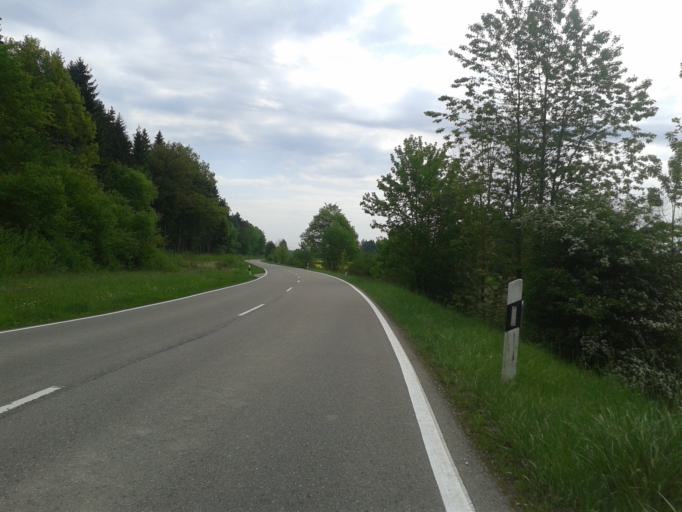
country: DE
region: Baden-Wuerttemberg
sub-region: Tuebingen Region
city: Erbach
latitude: 48.3542
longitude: 9.8484
